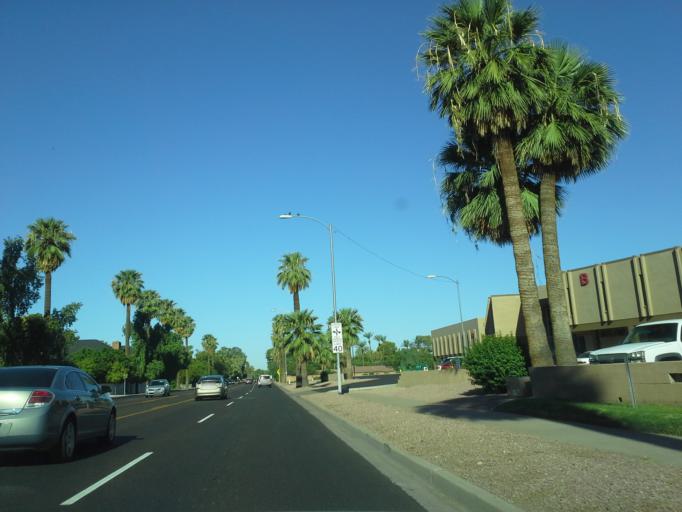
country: US
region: Arizona
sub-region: Maricopa County
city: Phoenix
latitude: 33.5384
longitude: -112.0747
